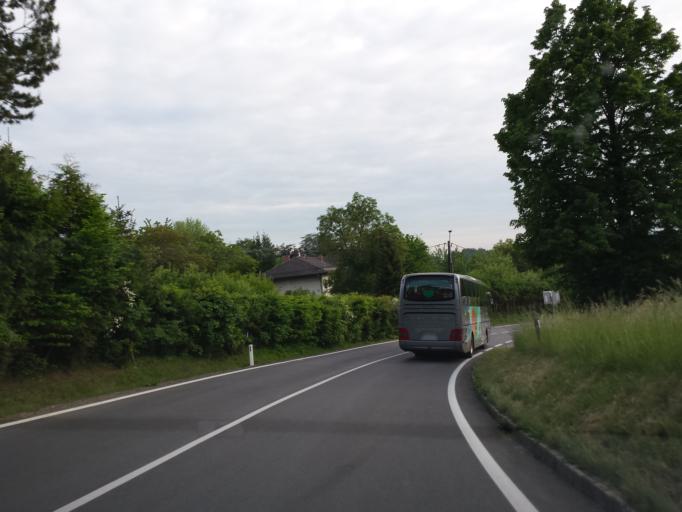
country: AT
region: Styria
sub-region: Graz Stadt
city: Mariatrost
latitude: 47.0943
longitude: 15.5201
